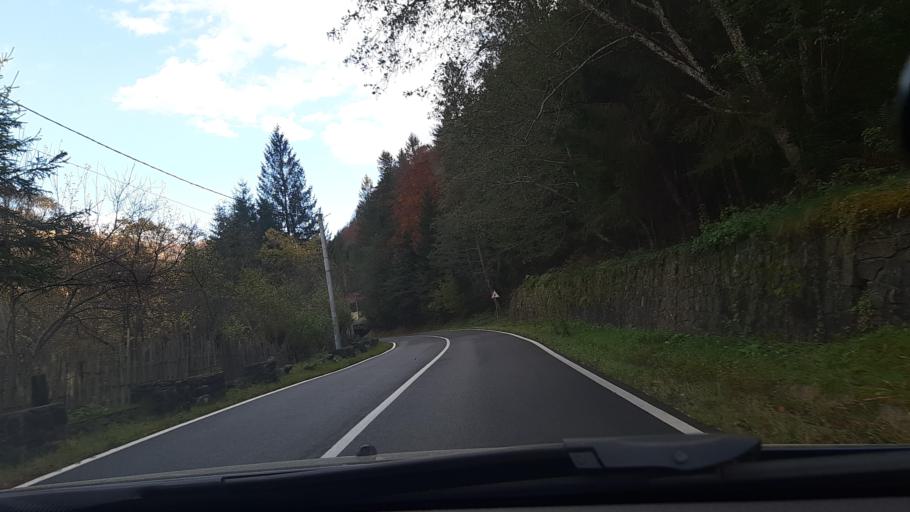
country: RO
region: Valcea
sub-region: Comuna Voineasa
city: Voineasa
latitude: 45.4071
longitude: 23.9752
